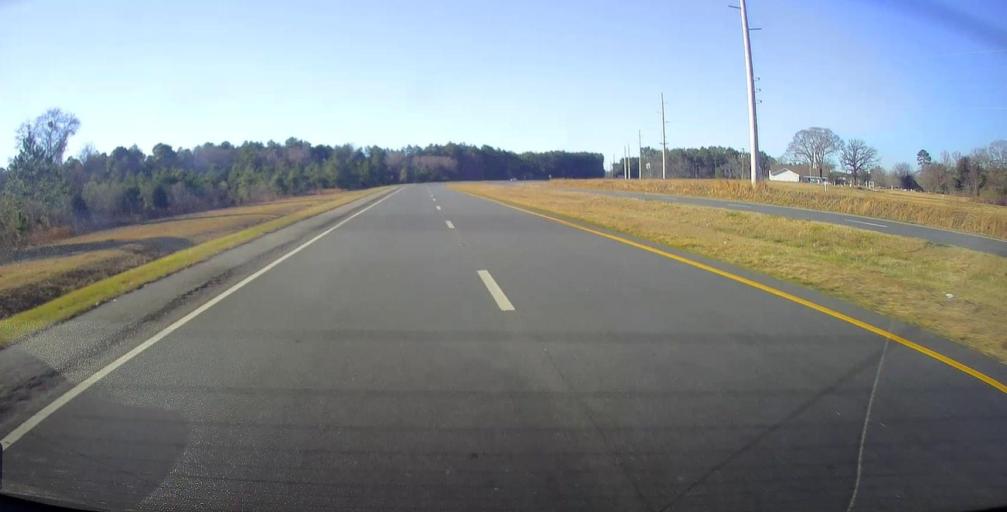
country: US
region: Georgia
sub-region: Lee County
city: Leesburg
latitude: 31.8129
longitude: -84.2115
